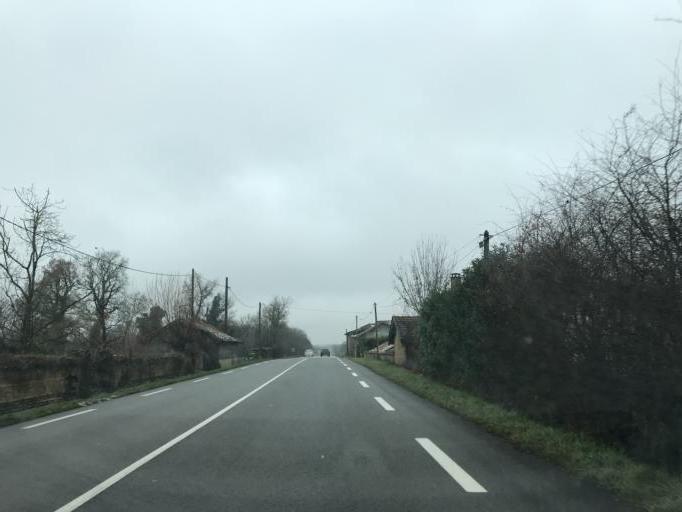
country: FR
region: Rhone-Alpes
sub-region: Departement de l'Ain
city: Saint-Paul-de-Varax
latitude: 46.0622
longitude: 5.0823
